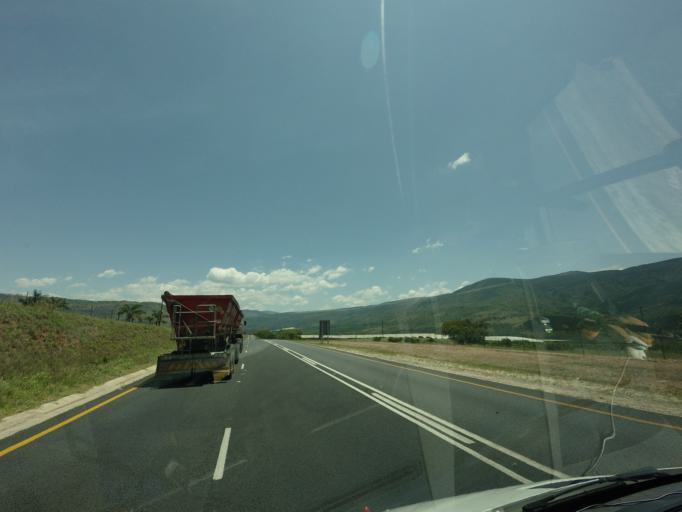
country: ZA
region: Mpumalanga
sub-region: Ehlanzeni District
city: Nelspruit
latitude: -25.4180
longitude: 30.6335
